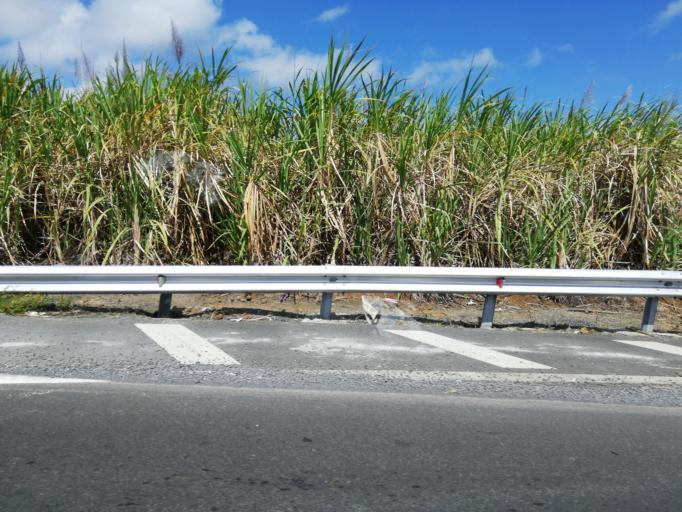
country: MU
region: Grand Port
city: Plaine Magnien
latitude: -20.4398
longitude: 57.6560
